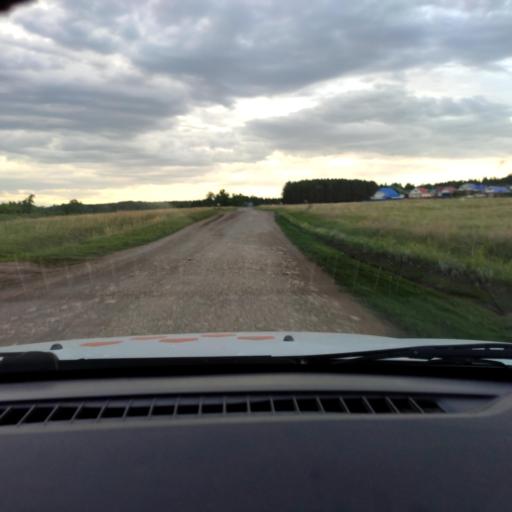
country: RU
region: Bashkortostan
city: Chishmy
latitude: 54.6098
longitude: 55.3955
